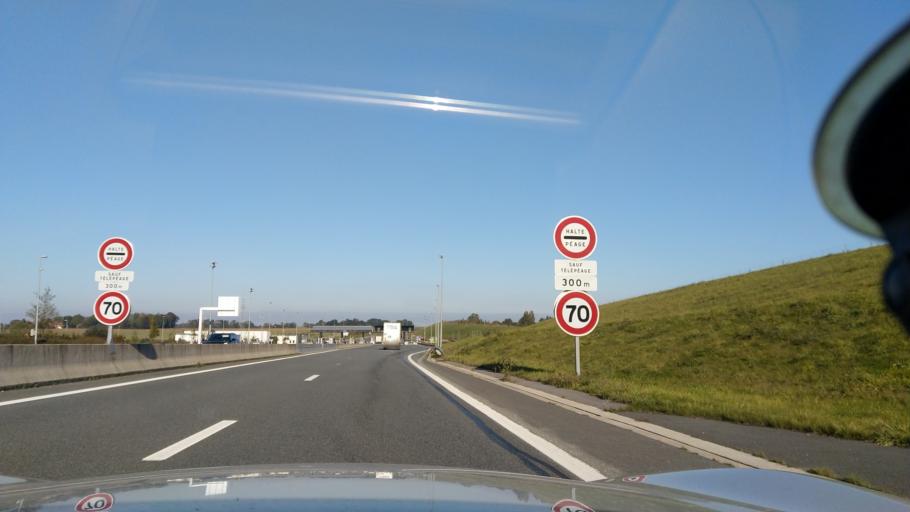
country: FR
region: Haute-Normandie
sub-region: Departement de la Seine-Maritime
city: Villers-Ecalles
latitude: 49.5456
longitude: 0.9248
